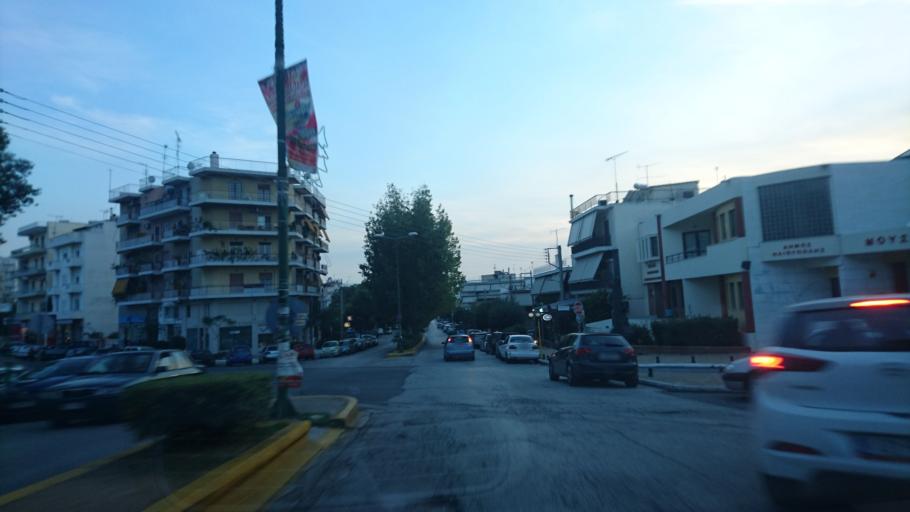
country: GR
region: Attica
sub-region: Nomarchia Athinas
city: Ilioupoli
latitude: 37.9313
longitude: 23.7556
